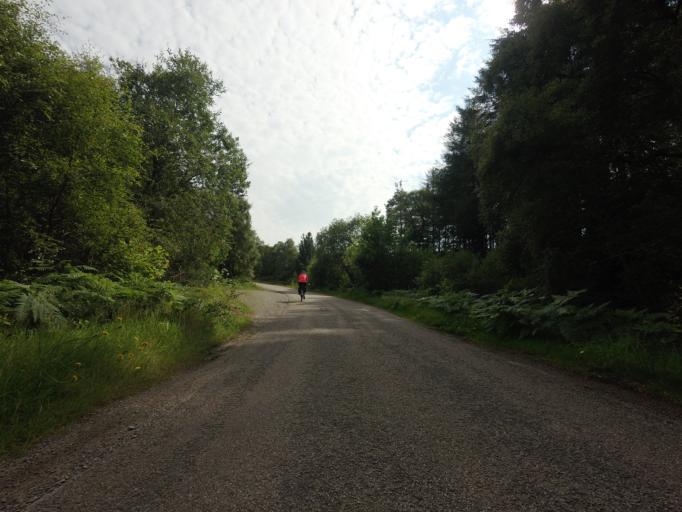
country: GB
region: Scotland
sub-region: Highland
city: Evanton
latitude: 57.9557
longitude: -4.4086
